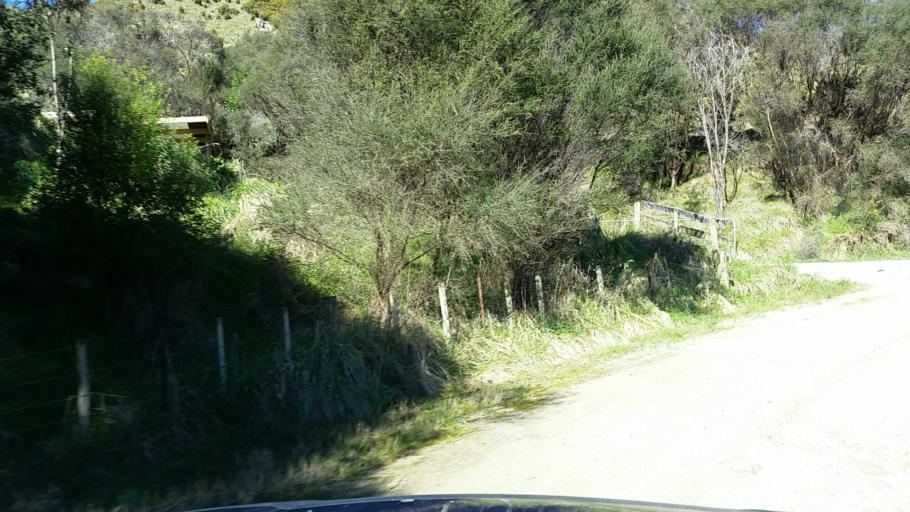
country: NZ
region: Manawatu-Wanganui
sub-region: Wanganui District
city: Wanganui
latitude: -39.6624
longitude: 174.8763
